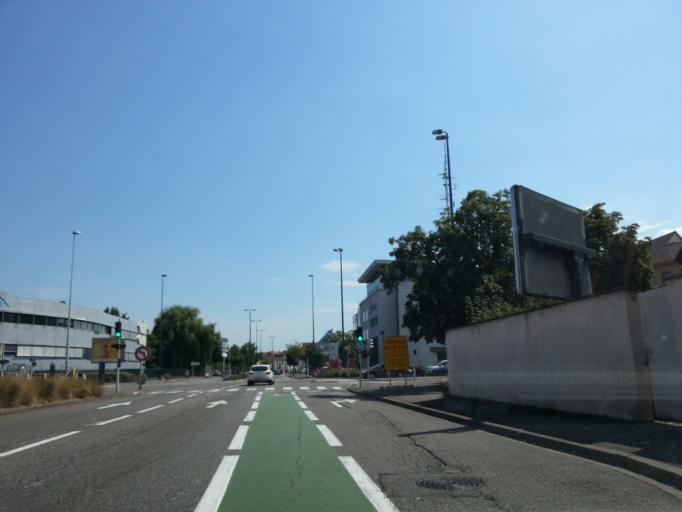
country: FR
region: Alsace
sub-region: Departement du Haut-Rhin
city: Colmar
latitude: 48.0771
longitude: 7.3658
